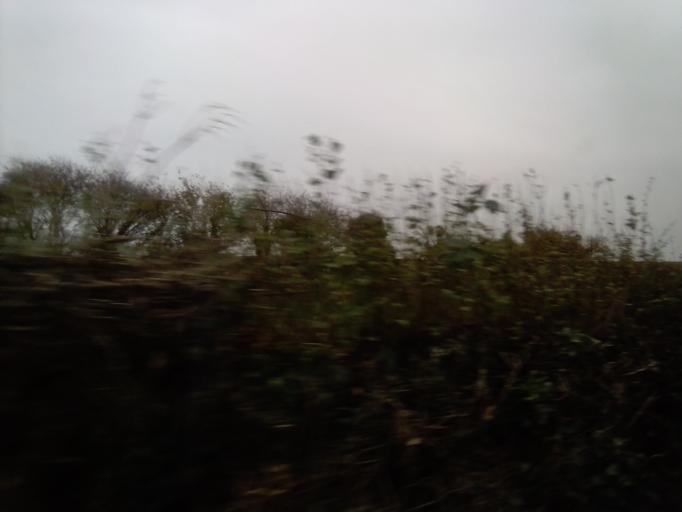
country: IE
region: Leinster
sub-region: Uibh Fhaili
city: Birr
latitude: 52.9737
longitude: -7.9734
